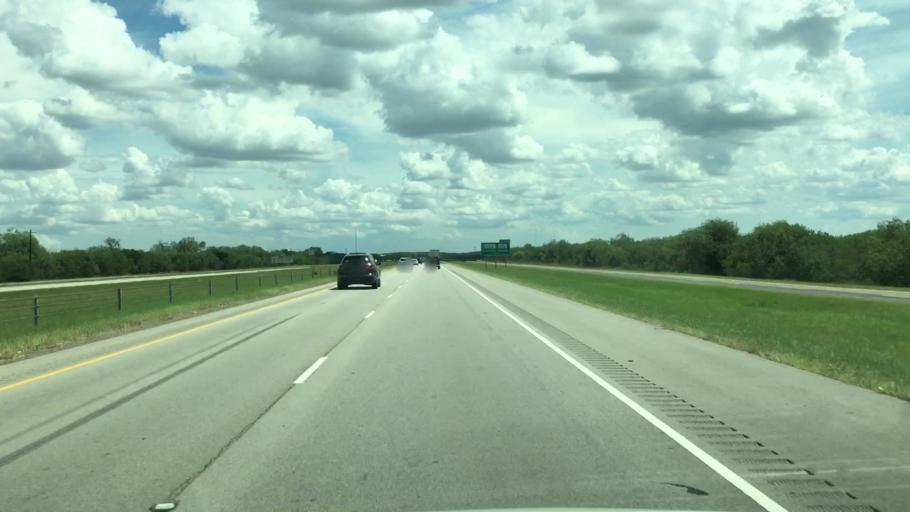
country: US
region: Texas
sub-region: Live Oak County
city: George West
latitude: 28.2761
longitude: -97.9504
